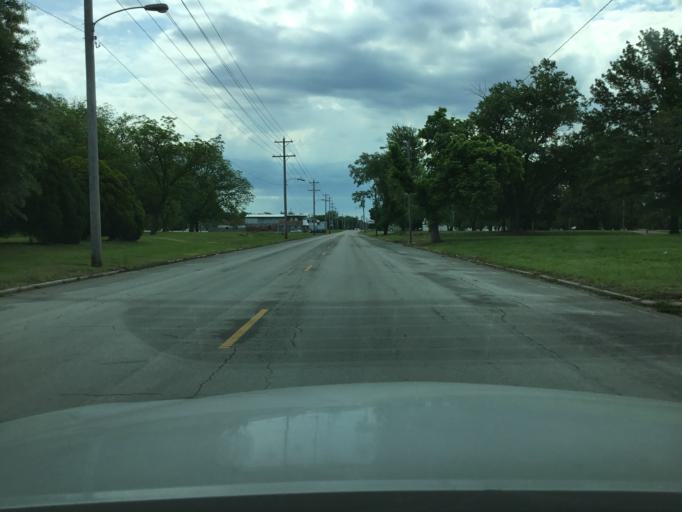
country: US
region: Kansas
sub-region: Montgomery County
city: Coffeyville
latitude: 37.0360
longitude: -95.6054
